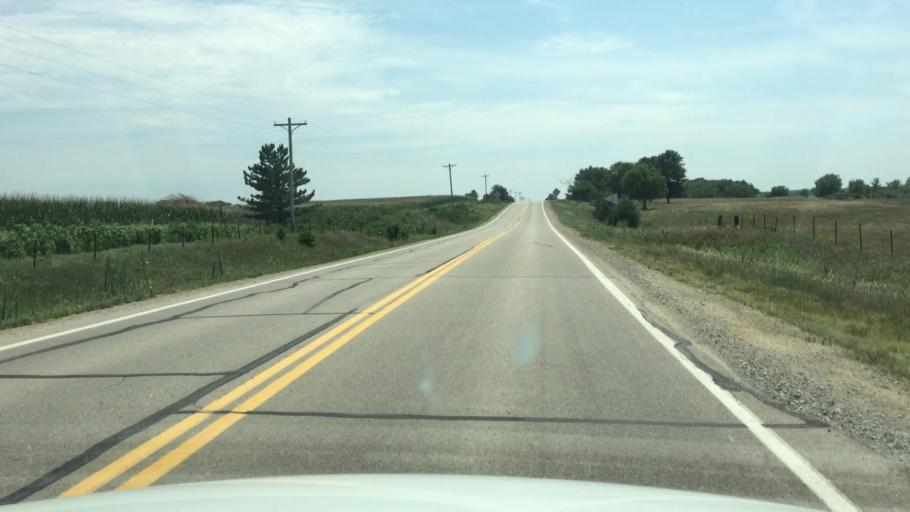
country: US
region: Kansas
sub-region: Shawnee County
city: Topeka
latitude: 38.9833
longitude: -95.4916
